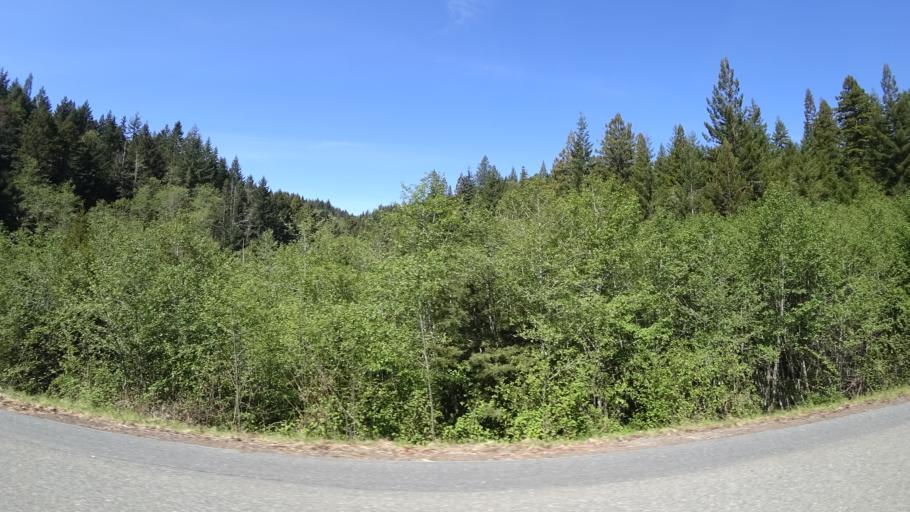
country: US
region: California
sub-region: Del Norte County
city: Bertsch-Oceanview
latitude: 41.4203
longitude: -123.9973
